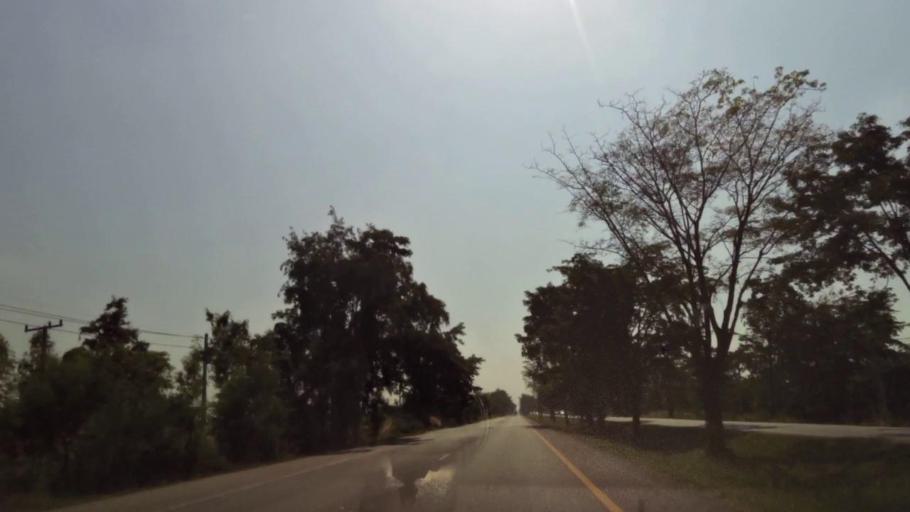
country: TH
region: Phichit
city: Bueng Na Rang
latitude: 16.2858
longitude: 100.1276
